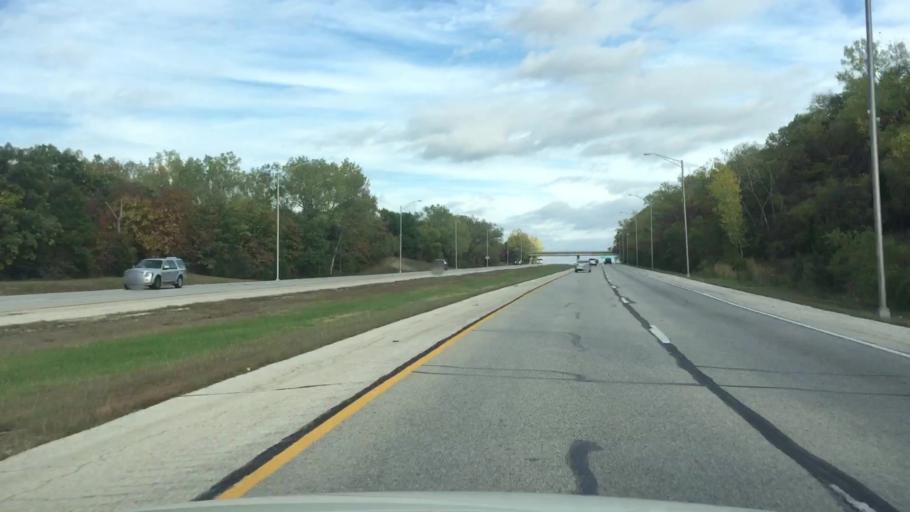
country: US
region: Kansas
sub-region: Wyandotte County
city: Edwardsville
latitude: 39.0104
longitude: -94.7988
